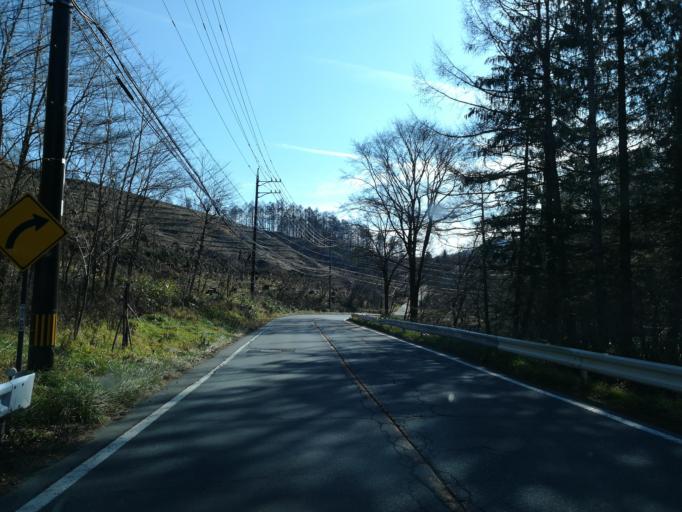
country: JP
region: Nagano
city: Ueda
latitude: 36.5173
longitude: 138.3402
